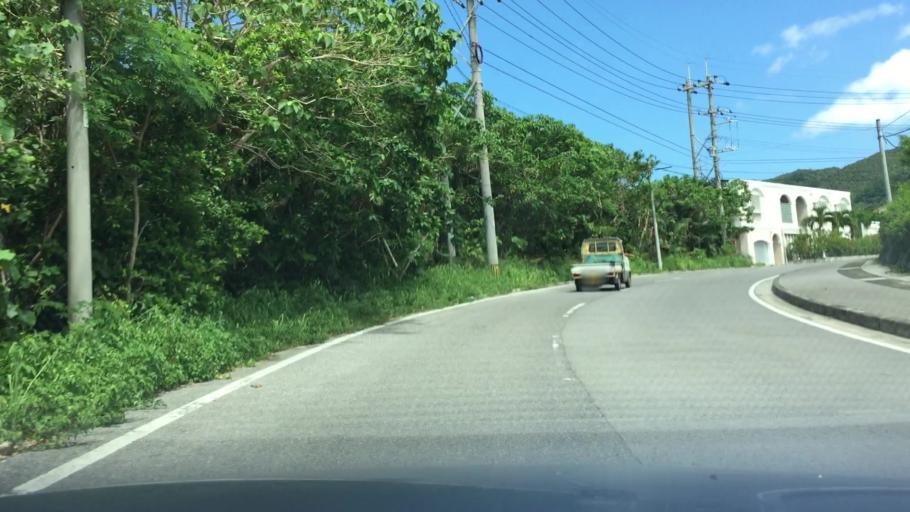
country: JP
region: Okinawa
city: Ishigaki
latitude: 24.4507
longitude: 124.1645
